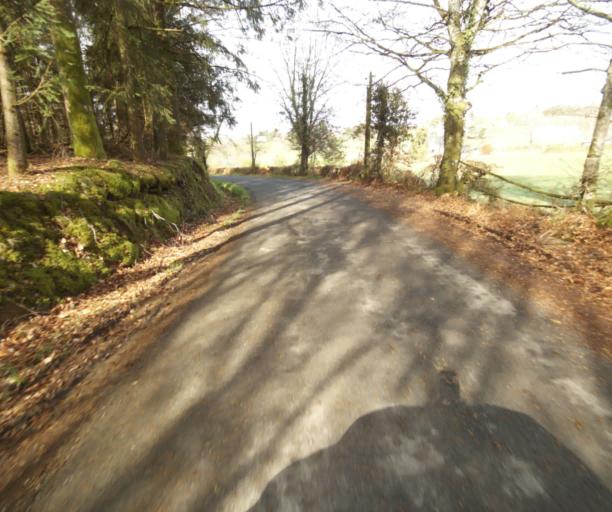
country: FR
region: Limousin
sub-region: Departement de la Correze
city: Laguenne
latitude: 45.2783
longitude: 1.8379
